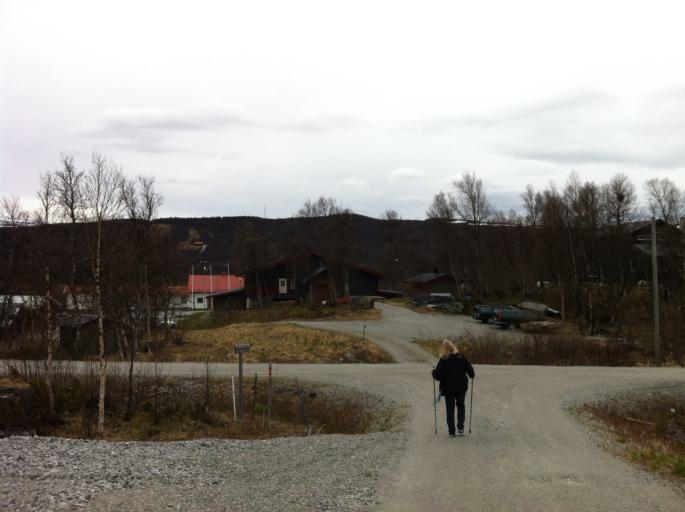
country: NO
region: Sor-Trondelag
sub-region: Tydal
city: Aas
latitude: 62.5503
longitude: 12.3100
